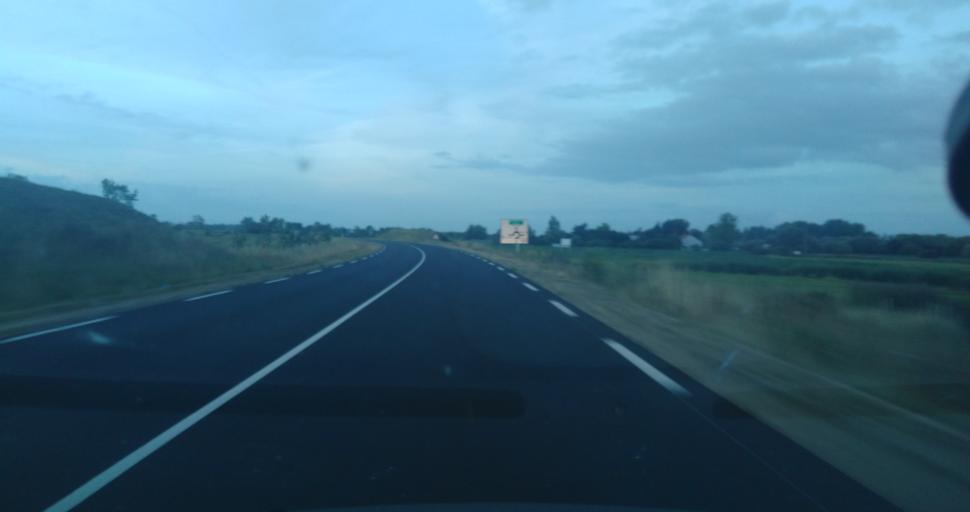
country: FR
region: Pays de la Loire
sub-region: Departement de la Vendee
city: Le Perrier
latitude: 46.8023
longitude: -1.9856
